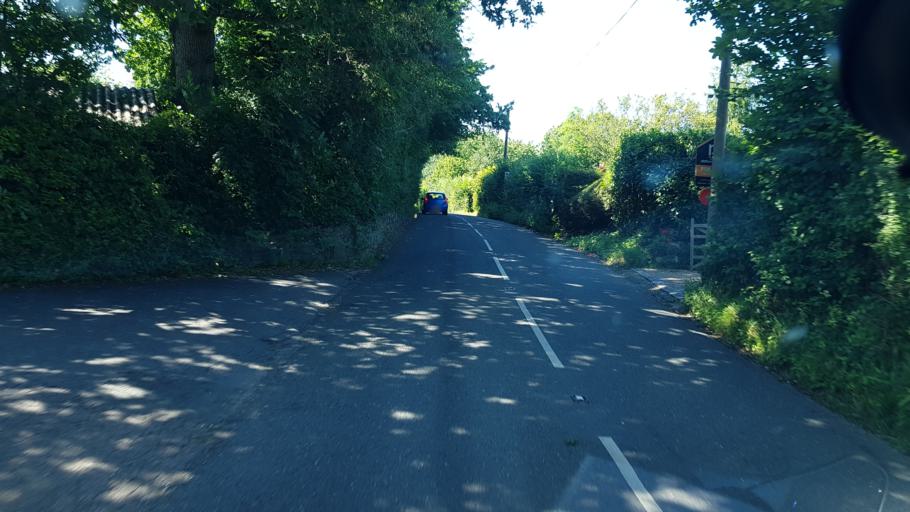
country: GB
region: England
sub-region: Kent
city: Westerham
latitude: 51.2349
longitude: 0.0656
